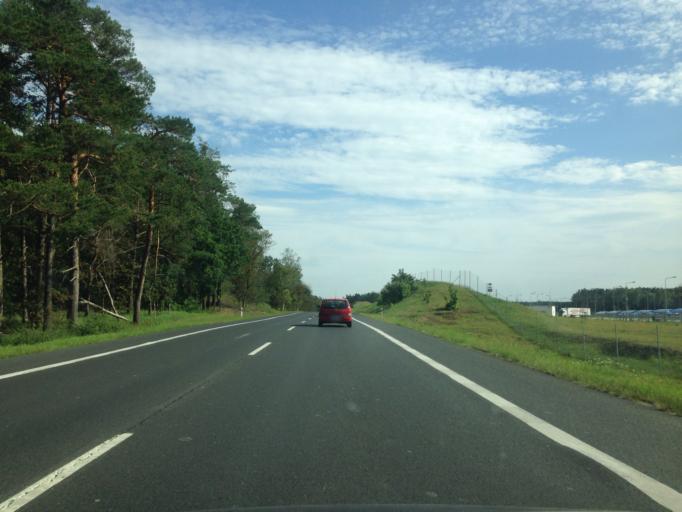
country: PL
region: Kujawsko-Pomorskie
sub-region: Powiat aleksandrowski
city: Aleksandrow Kujawski
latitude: 52.9038
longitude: 18.7234
